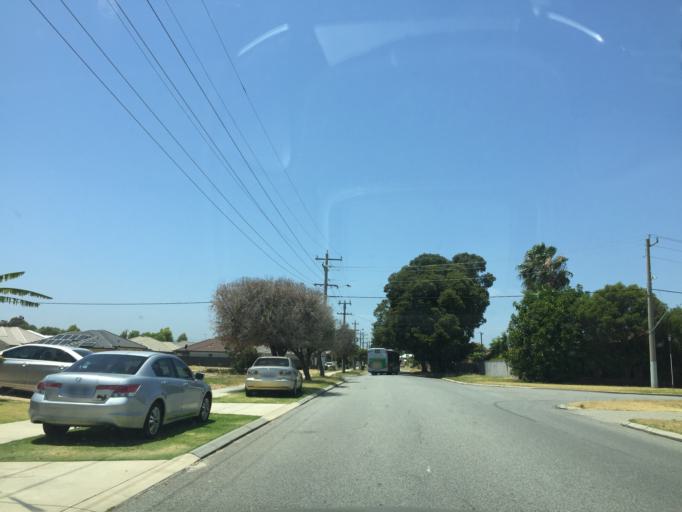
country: AU
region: Western Australia
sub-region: Canning
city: Queens Park
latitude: -32.0094
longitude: 115.9436
